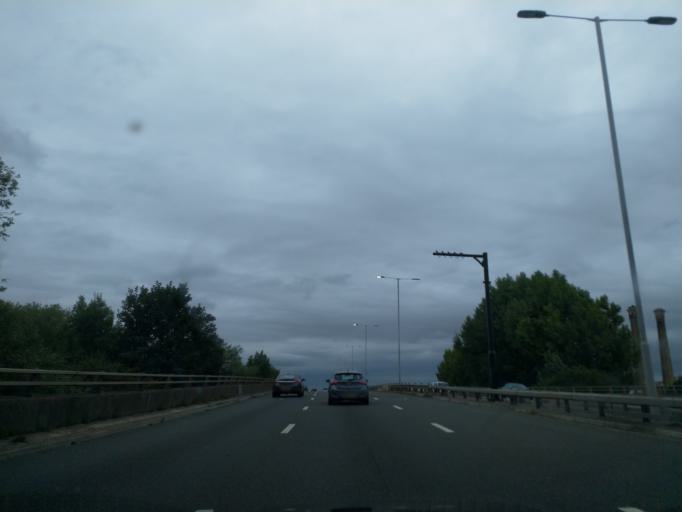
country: GB
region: England
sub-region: Greater London
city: Feltham
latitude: 51.4245
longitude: -0.4069
